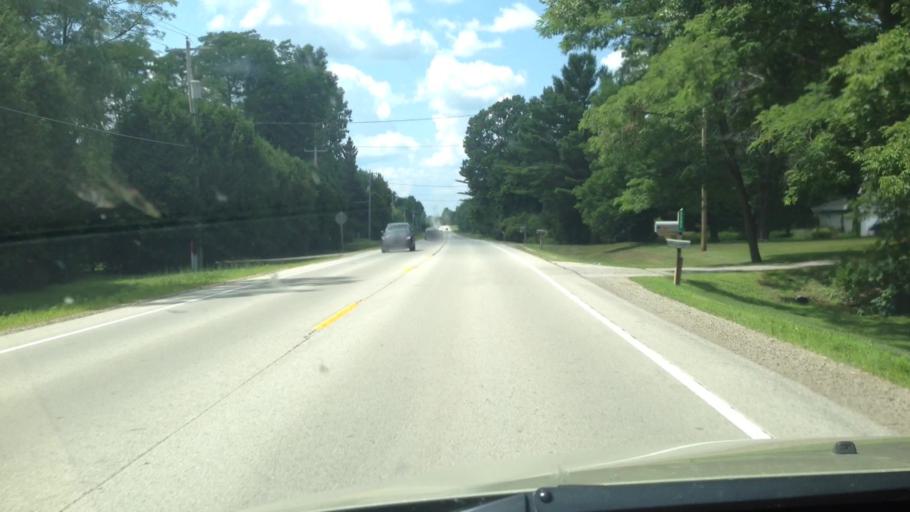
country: US
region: Wisconsin
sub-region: Brown County
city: Suamico
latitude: 44.6393
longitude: -88.0727
